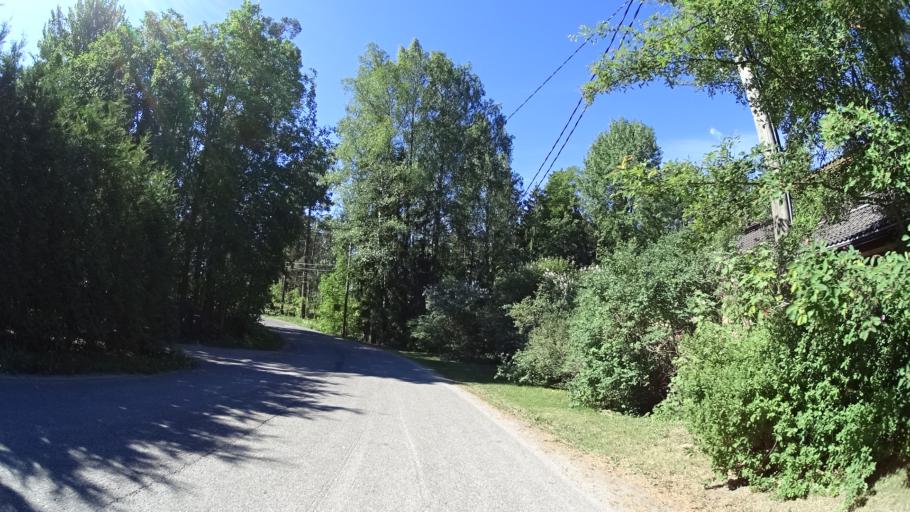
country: FI
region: Uusimaa
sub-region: Helsinki
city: Kauniainen
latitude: 60.2030
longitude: 24.7220
